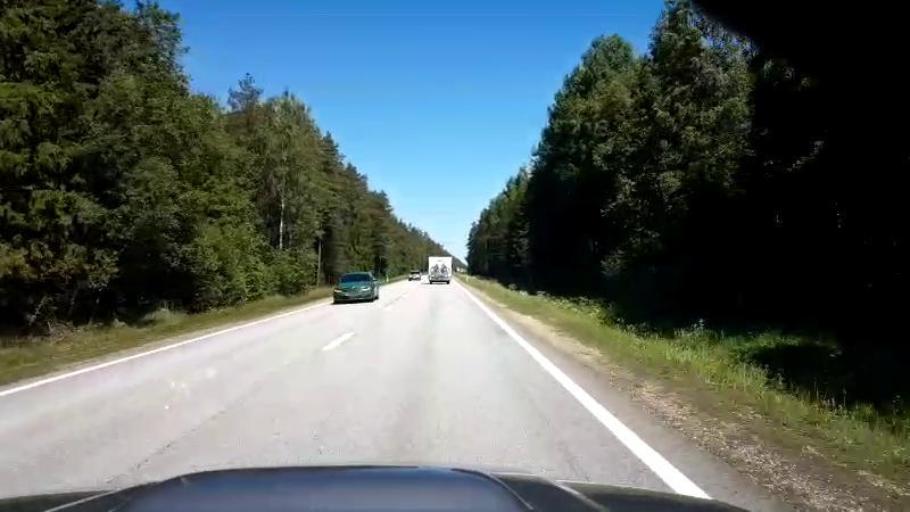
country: LV
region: Salacgrivas
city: Salacgriva
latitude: 57.5309
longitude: 24.4308
